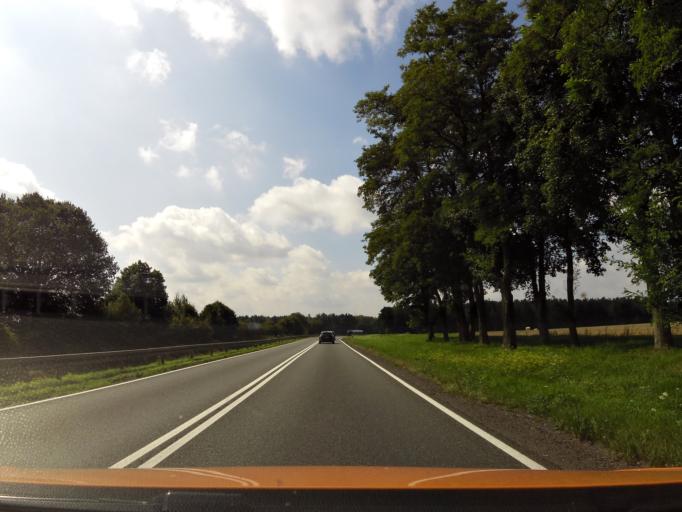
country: PL
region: West Pomeranian Voivodeship
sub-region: Powiat goleniowski
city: Nowogard
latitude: 53.7018
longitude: 15.1686
